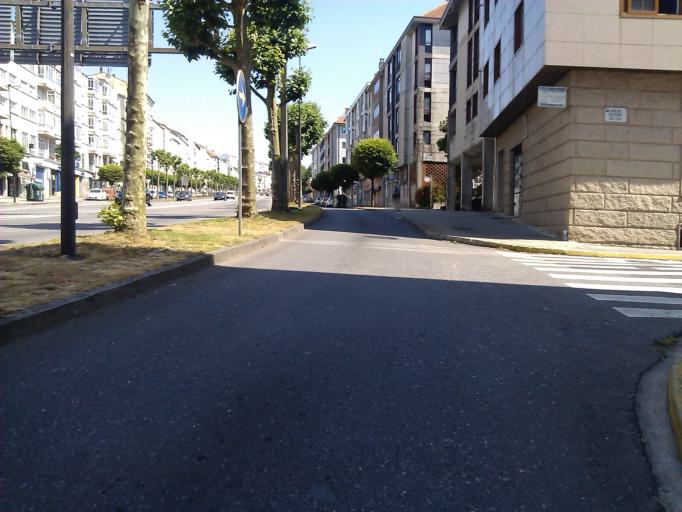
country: ES
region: Galicia
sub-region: Provincia da Coruna
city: Santiago de Compostela
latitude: 42.8797
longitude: -8.5328
